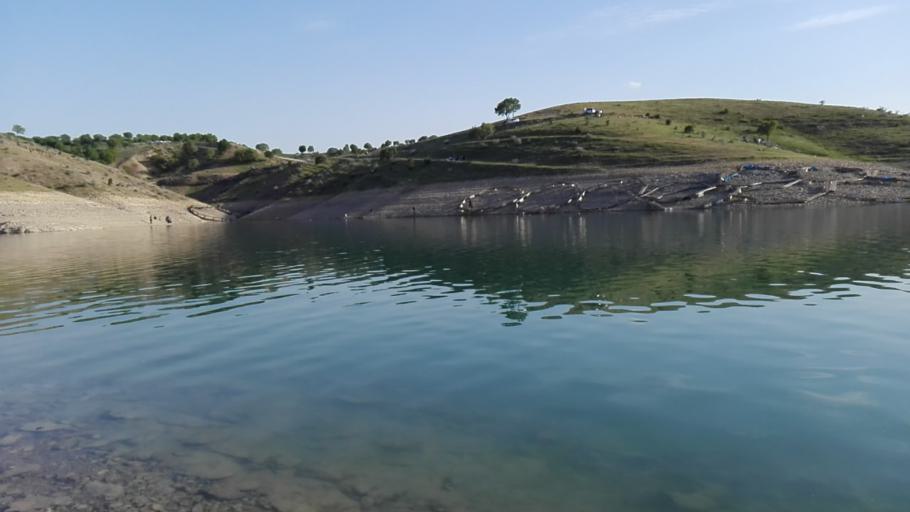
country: TR
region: Diyarbakir
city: Malabadi
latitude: 38.1773
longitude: 41.2169
